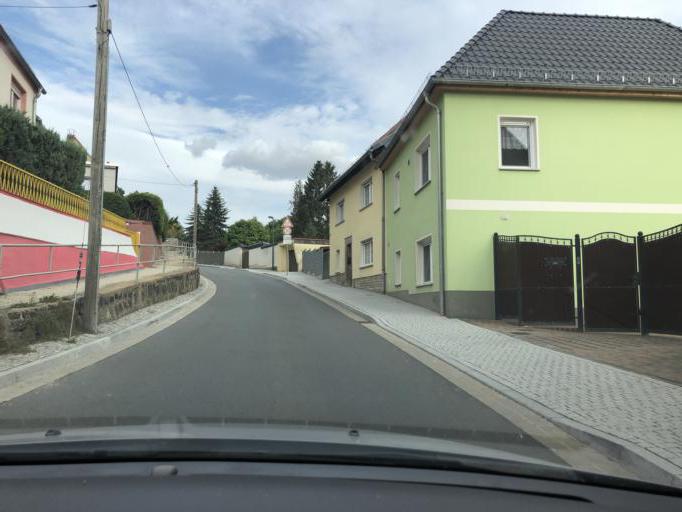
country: DE
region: Saxony-Anhalt
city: Osterfeld
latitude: 51.0777
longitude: 11.9312
